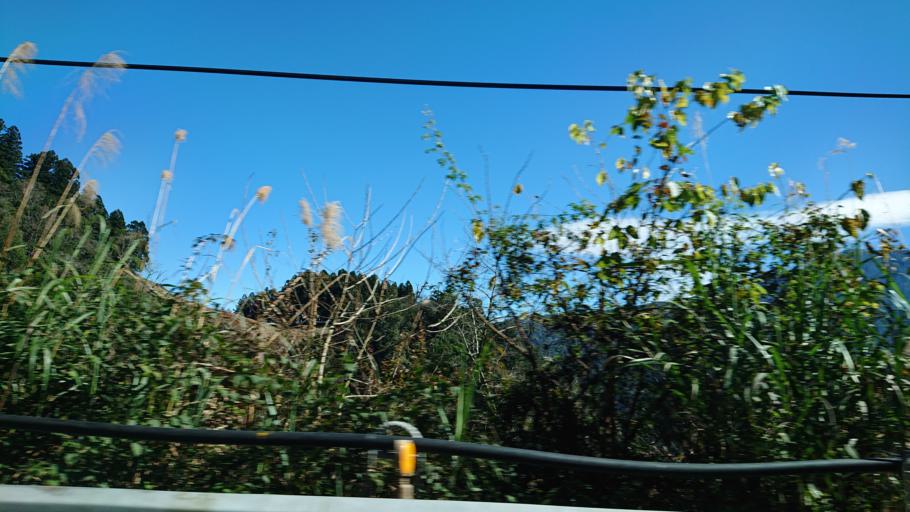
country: TW
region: Taiwan
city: Daxi
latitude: 24.4137
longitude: 121.3638
